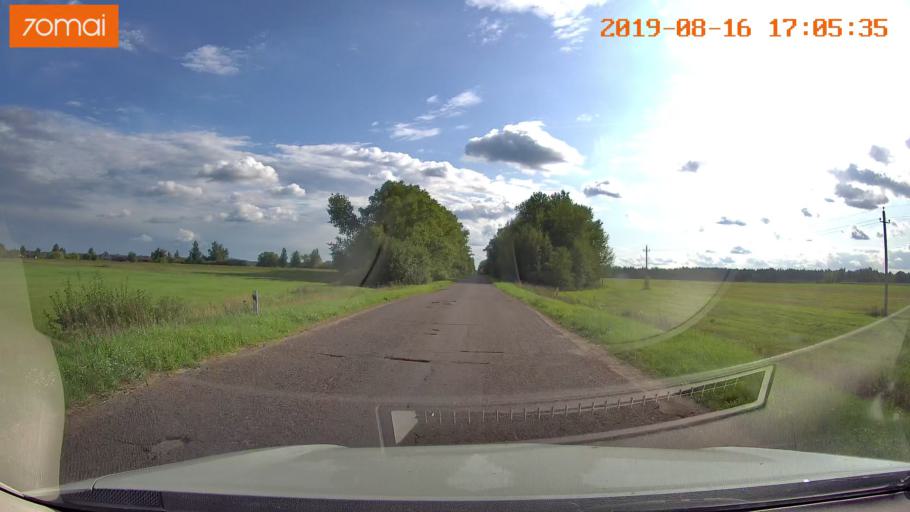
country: BY
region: Mogilev
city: Hlusha
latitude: 53.2360
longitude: 28.9426
